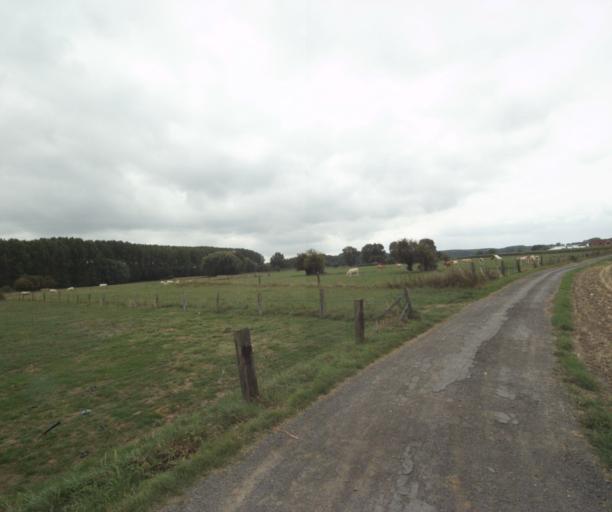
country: FR
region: Nord-Pas-de-Calais
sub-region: Departement du Nord
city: Forest-sur-Marque
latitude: 50.6333
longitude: 3.2041
